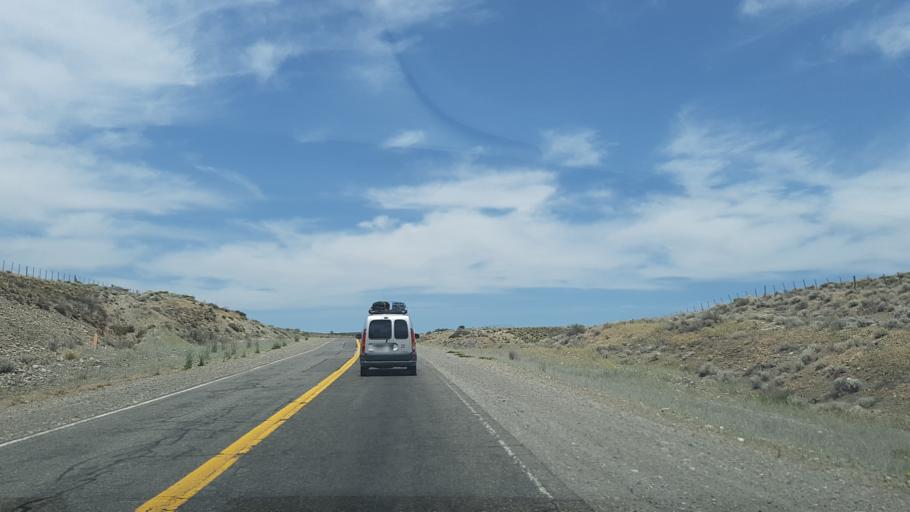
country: AR
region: Rio Negro
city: Pilcaniyeu
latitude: -40.4889
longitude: -70.6802
